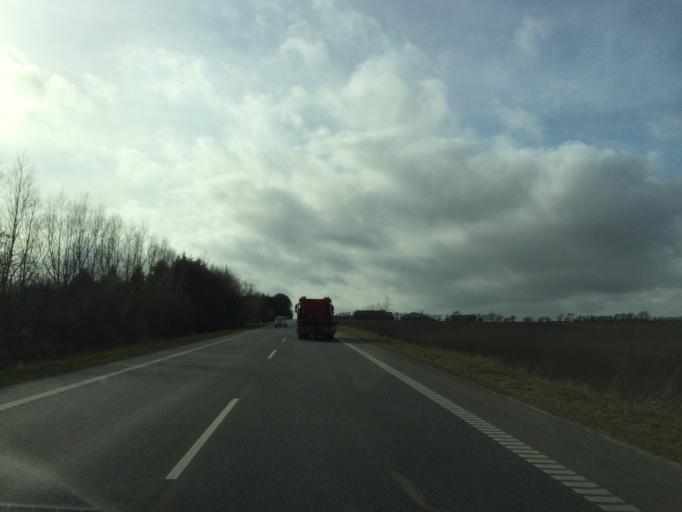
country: DK
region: Central Jutland
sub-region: Randers Kommune
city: Langa
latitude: 56.4750
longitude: 9.9306
